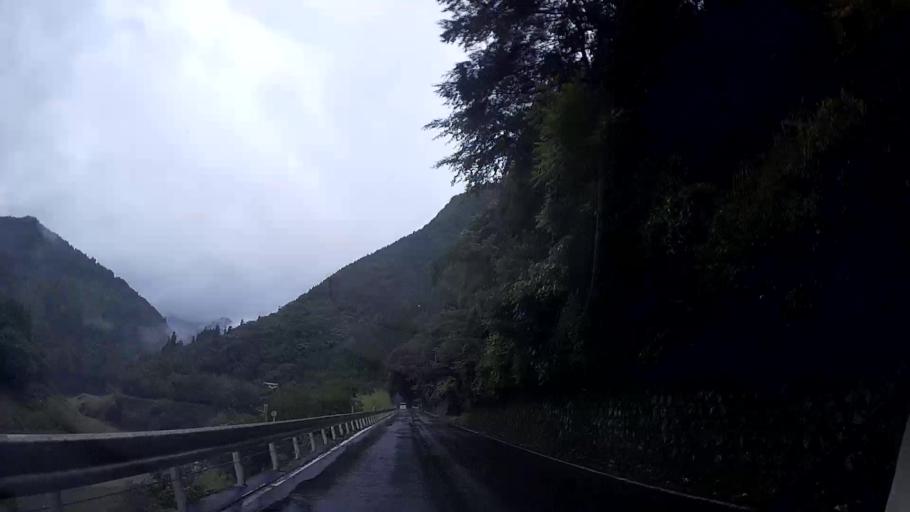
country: JP
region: Oita
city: Hita
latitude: 33.1787
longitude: 131.0133
